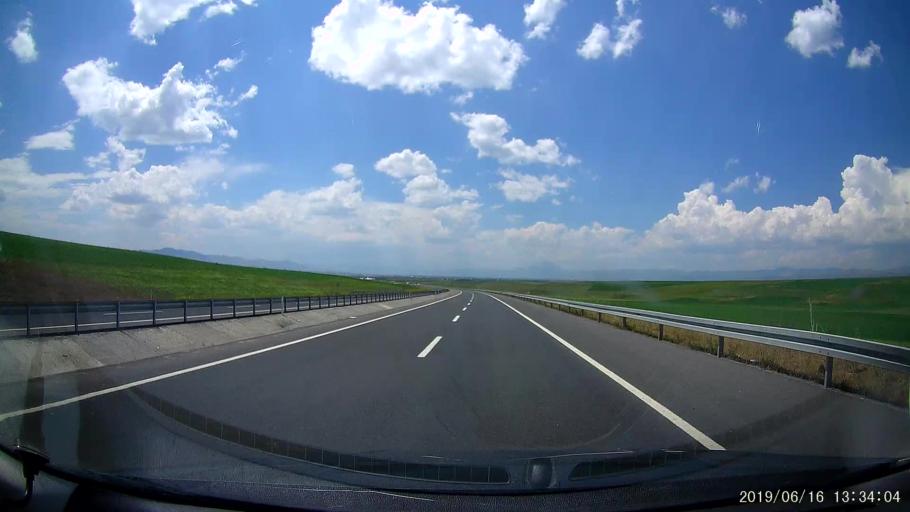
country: TR
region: Agri
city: Agri
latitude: 39.7109
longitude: 43.1372
